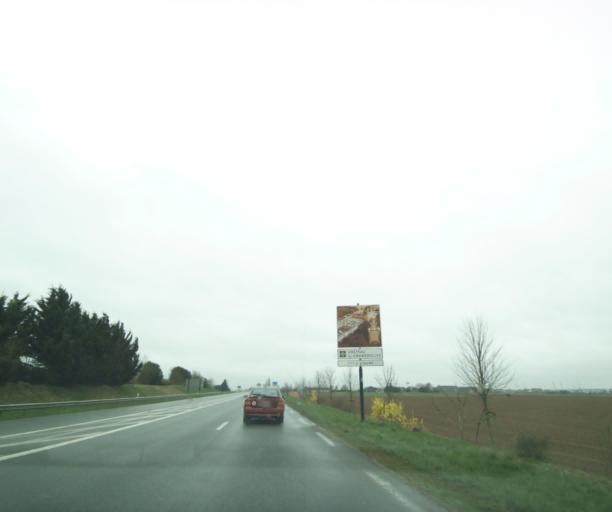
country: FR
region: Centre
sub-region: Departement du Loiret
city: Artenay
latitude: 48.0880
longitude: 1.8773
